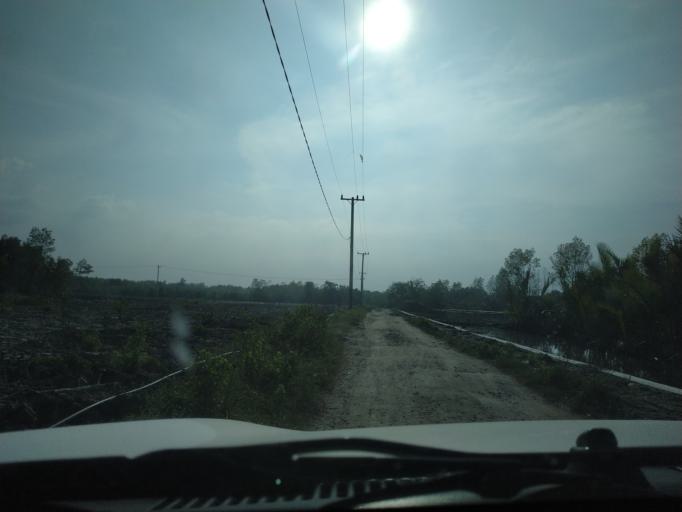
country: ID
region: North Sumatra
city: Teluk Nibung
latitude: 3.1028
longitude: 99.7758
